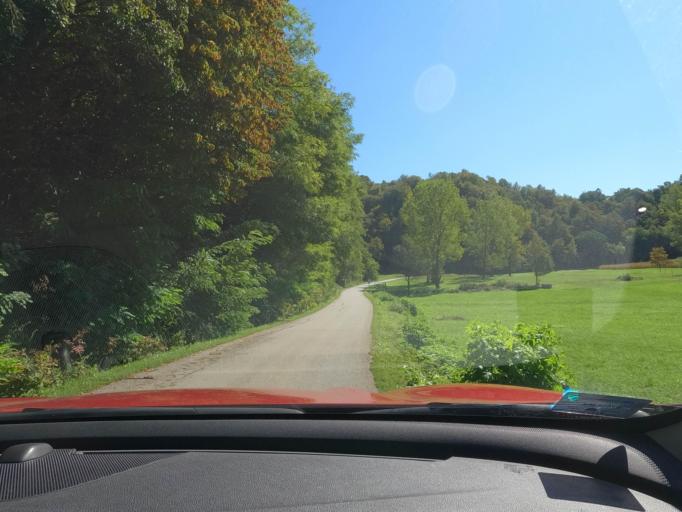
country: HR
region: Sisacko-Moslavacka
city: Petrinja
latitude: 45.3888
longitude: 16.2476
